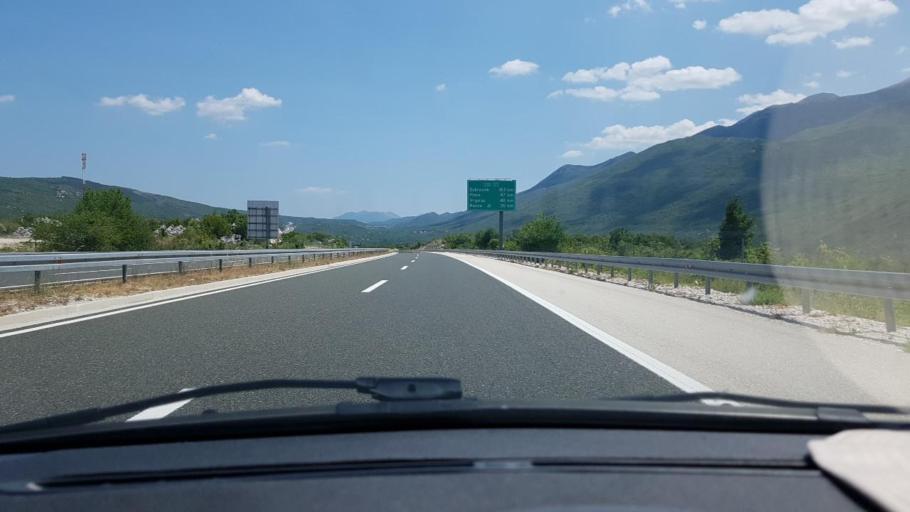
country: HR
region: Splitsko-Dalmatinska
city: Baska Voda
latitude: 43.3988
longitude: 17.0358
